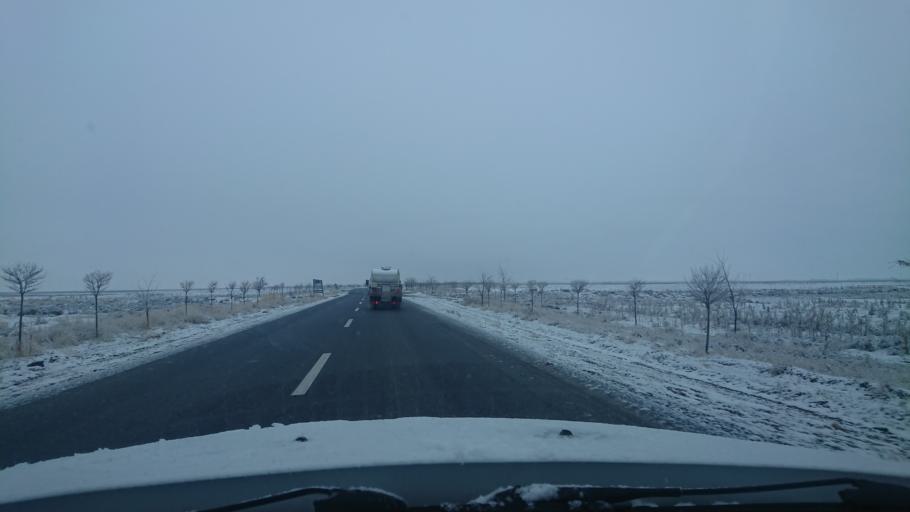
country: TR
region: Aksaray
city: Yesilova
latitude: 38.3089
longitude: 33.7544
